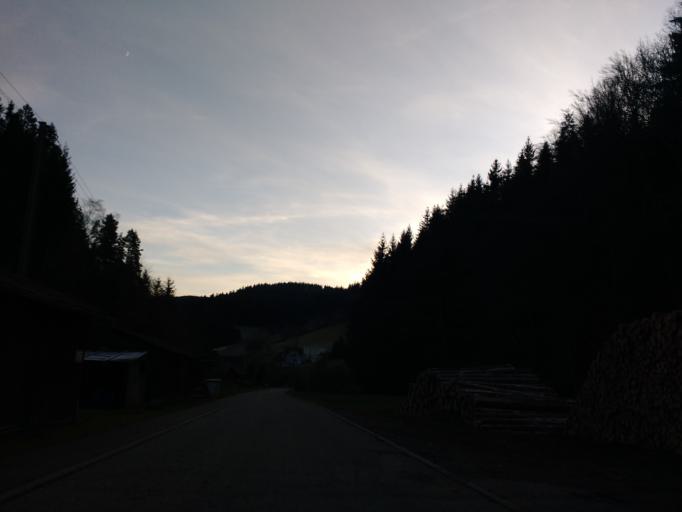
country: DE
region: Baden-Wuerttemberg
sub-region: Karlsruhe Region
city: Bad Rippoldsau-Schapbach
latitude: 48.4555
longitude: 8.2875
